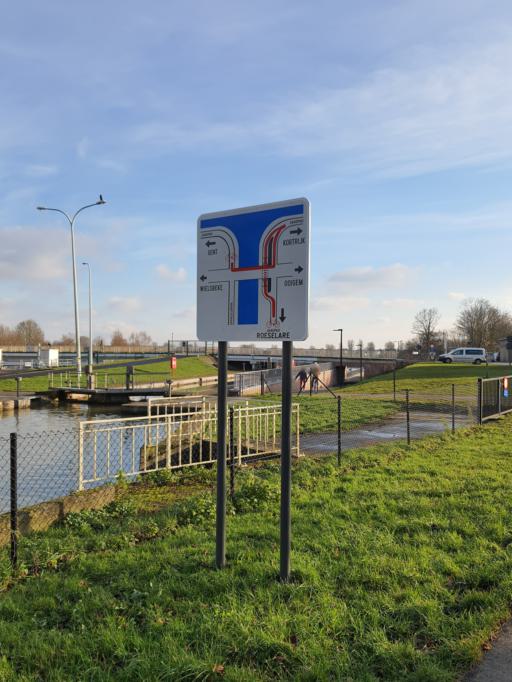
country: BE
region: Flanders
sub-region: Provincie West-Vlaanderen
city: Wielsbeke
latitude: 50.8971
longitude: 3.3432
